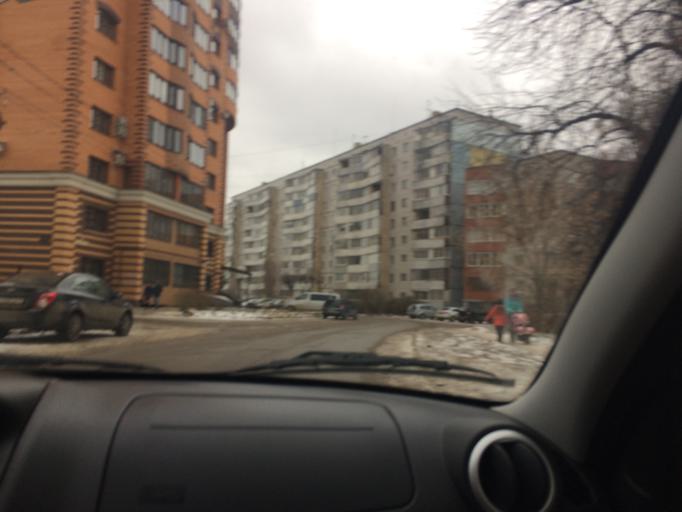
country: RU
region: Rjazan
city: Ryazan'
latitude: 54.6213
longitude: 39.7140
